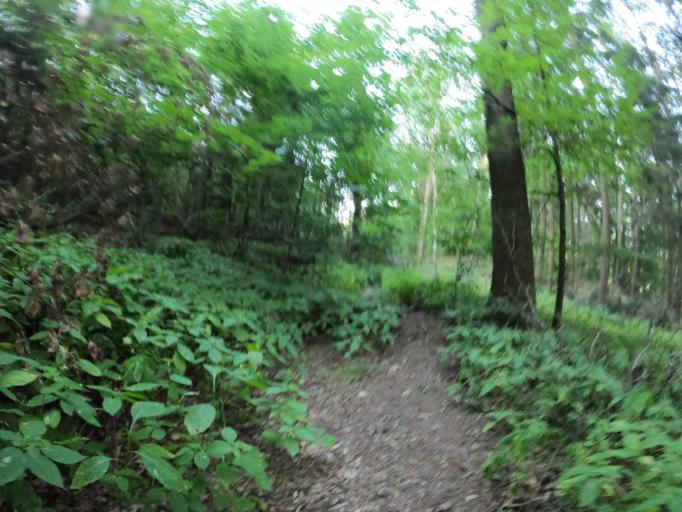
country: PL
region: West Pomeranian Voivodeship
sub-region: Powiat drawski
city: Zlocieniec
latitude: 53.6505
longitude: 15.9213
